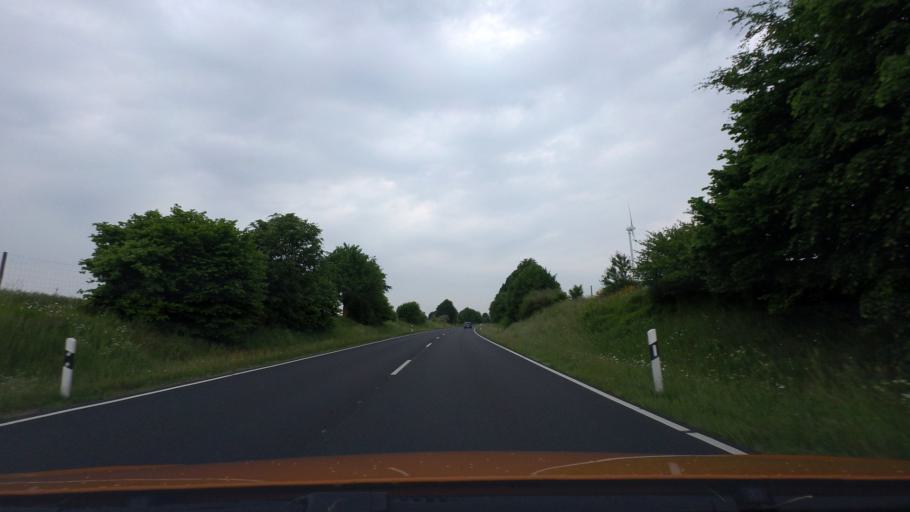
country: DE
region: Lower Saxony
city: Wietzen
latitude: 52.6645
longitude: 9.1029
